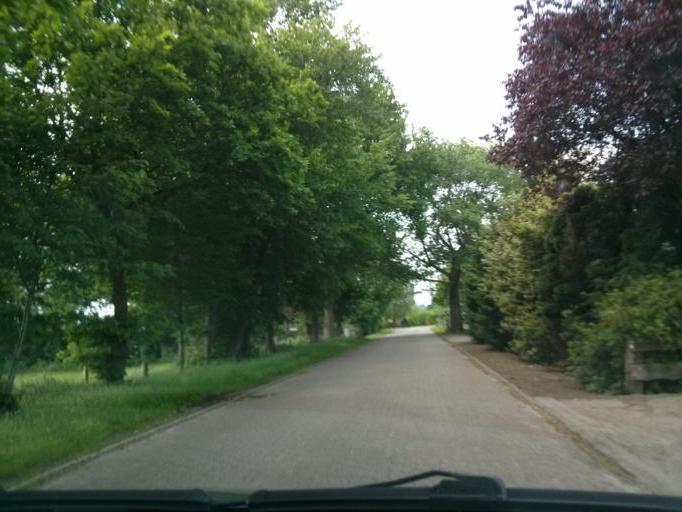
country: DE
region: Lower Saxony
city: Schiffdorf
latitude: 53.5080
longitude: 8.6961
